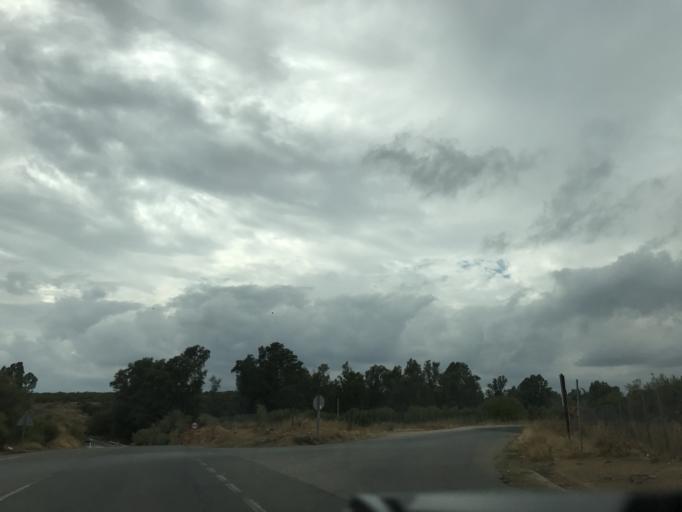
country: ES
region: Andalusia
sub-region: Provincia de Sevilla
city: Villanueva del Rio y Minas
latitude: 37.6433
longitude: -5.7417
